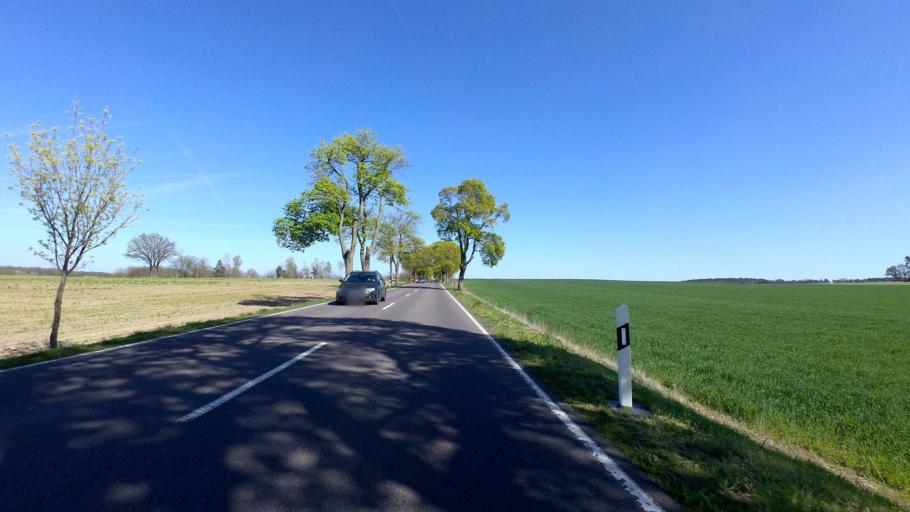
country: DE
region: Saxony-Anhalt
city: Kalbe
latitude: 52.6486
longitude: 11.3008
